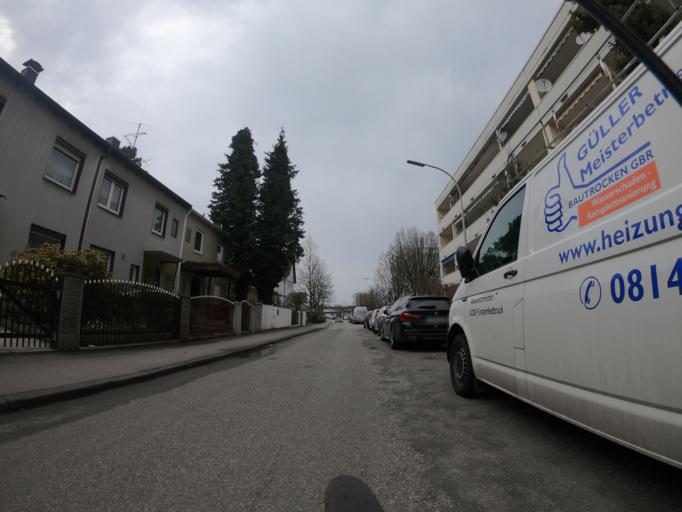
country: DE
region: Bavaria
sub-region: Upper Bavaria
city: Fuerstenfeldbruck
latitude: 48.1771
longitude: 11.2335
